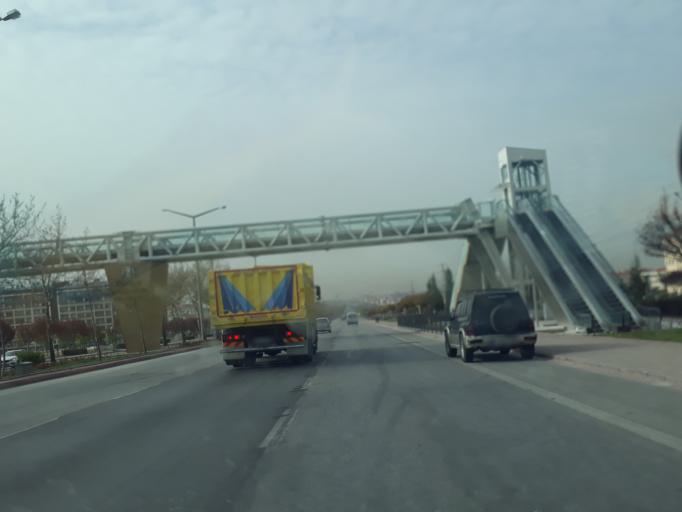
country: TR
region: Konya
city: Asagipinarbasi
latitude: 37.9876
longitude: 32.5178
